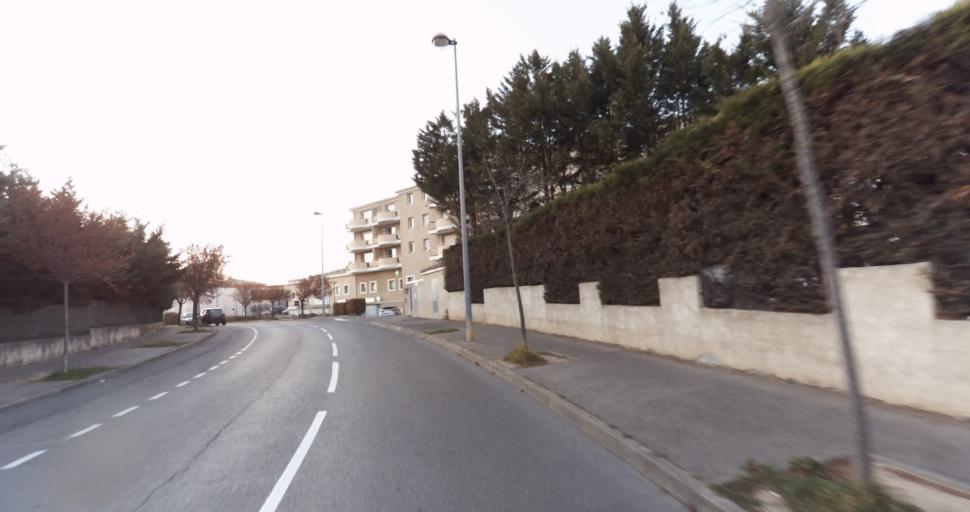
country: FR
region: Provence-Alpes-Cote d'Azur
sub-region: Departement des Bouches-du-Rhone
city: Aix-en-Provence
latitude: 43.5339
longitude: 5.4107
